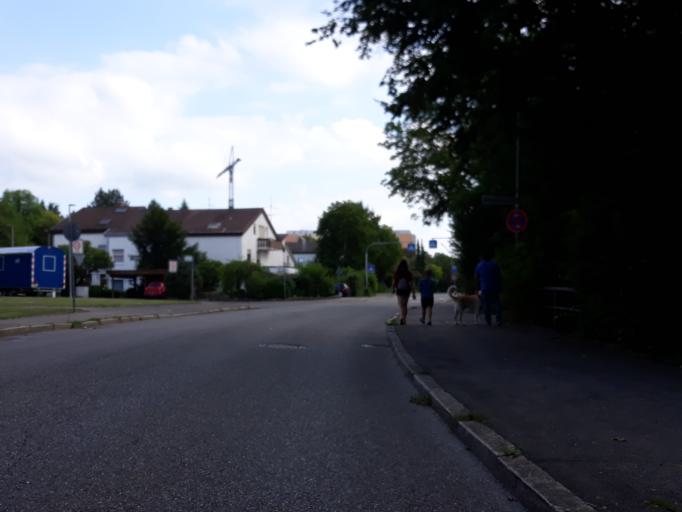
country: DE
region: Baden-Wuerttemberg
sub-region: Regierungsbezirk Stuttgart
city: Boeblingen
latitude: 48.6805
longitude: 9.0271
